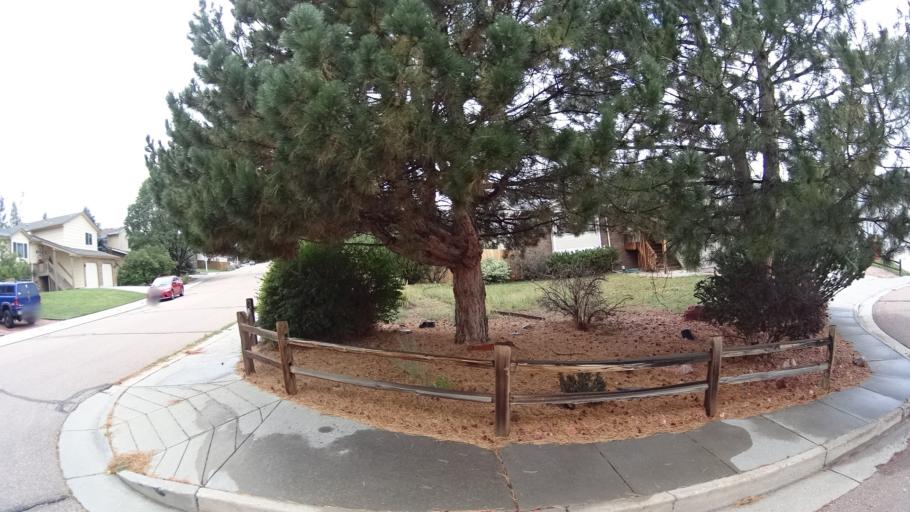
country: US
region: Colorado
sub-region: El Paso County
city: Cimarron Hills
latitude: 38.9238
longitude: -104.7602
